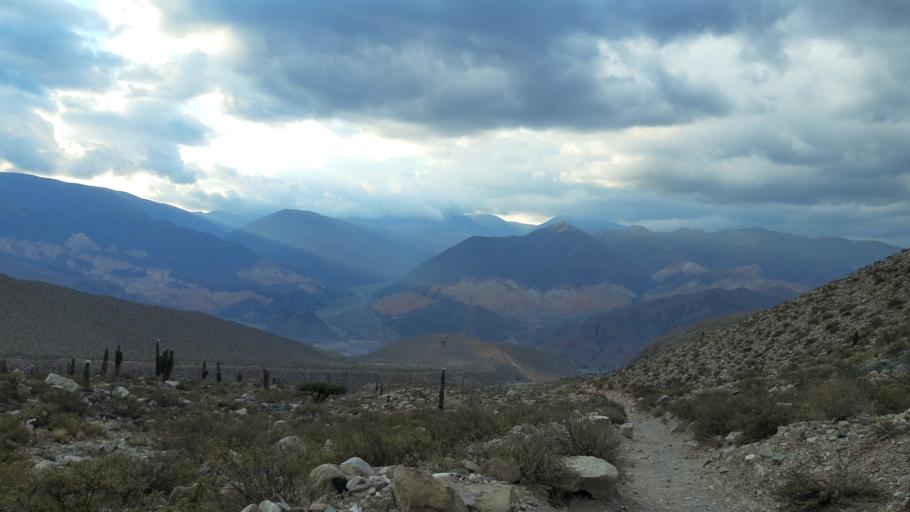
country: AR
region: Jujuy
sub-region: Departamento de Tilcara
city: Tilcara
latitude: -23.5930
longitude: -65.3811
